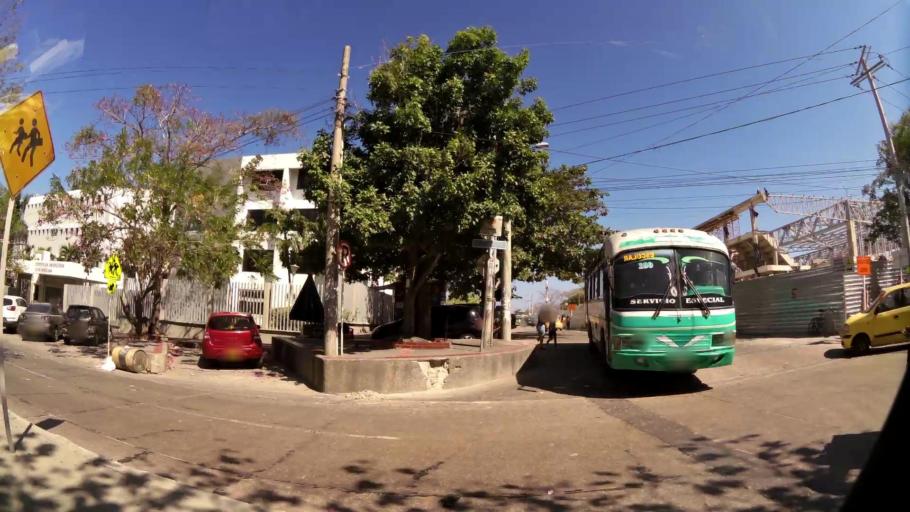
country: CO
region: Atlantico
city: Barranquilla
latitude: 10.9944
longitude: -74.7914
